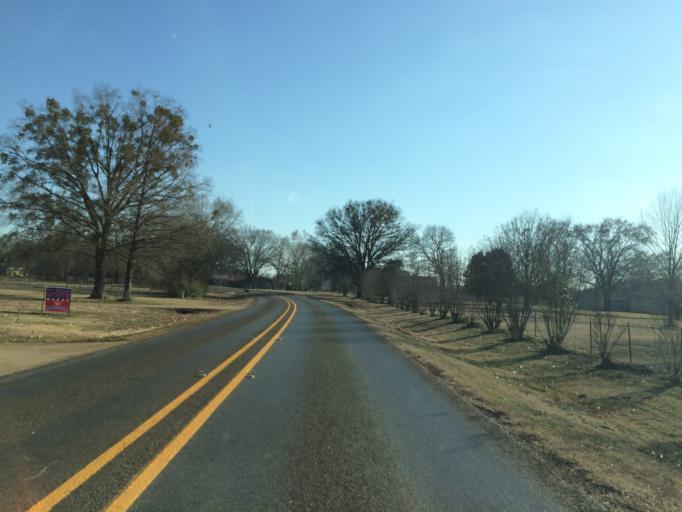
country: US
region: Texas
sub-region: Wood County
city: Quitman
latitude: 32.7164
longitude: -95.3660
